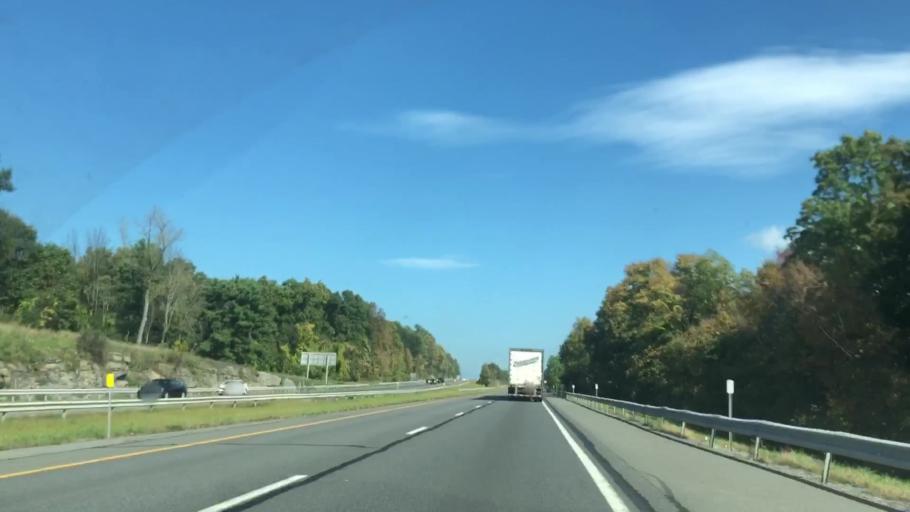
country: US
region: New York
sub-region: Greene County
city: Jefferson Heights
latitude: 42.2587
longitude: -73.8785
